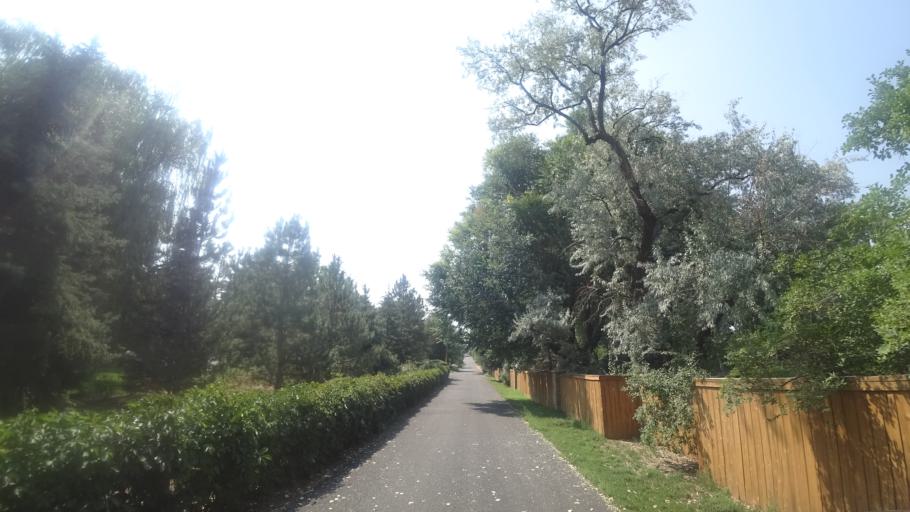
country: US
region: Colorado
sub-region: Arapahoe County
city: Cherry Hills Village
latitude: 39.6351
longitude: -104.9658
